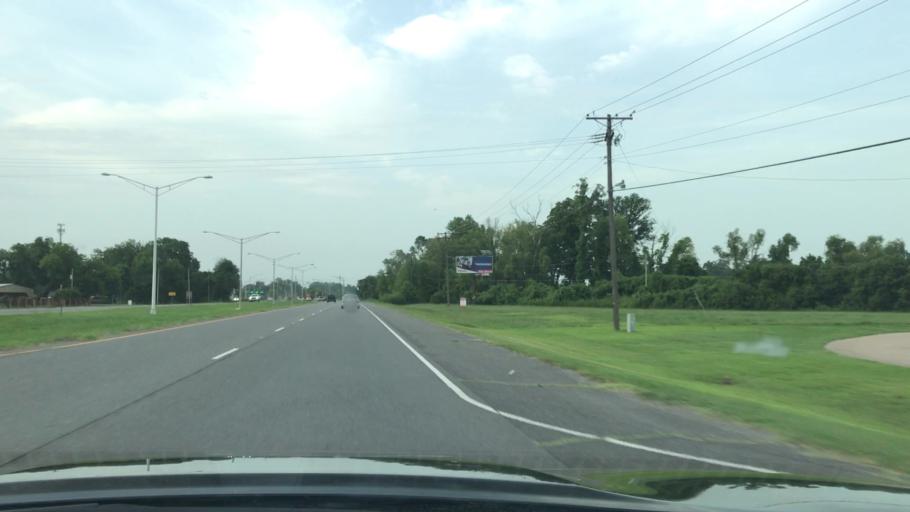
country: US
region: Louisiana
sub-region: Bossier Parish
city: Bossier City
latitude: 32.4054
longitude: -93.6968
